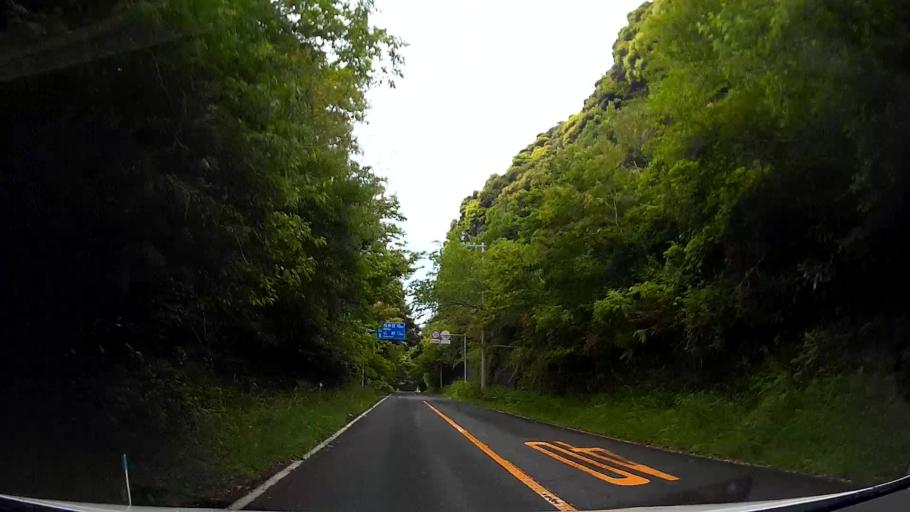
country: JP
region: Shizuoka
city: Shimoda
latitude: 34.7010
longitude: 138.7590
